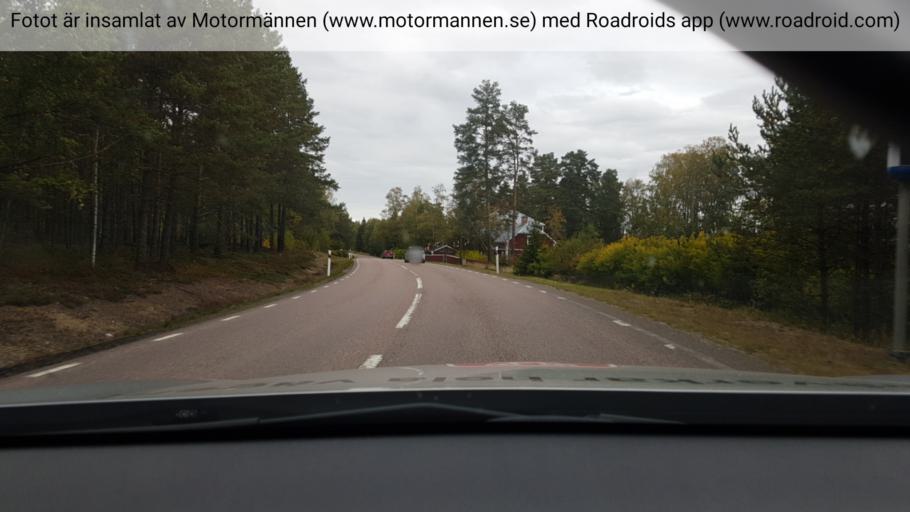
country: SE
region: Gaevleborg
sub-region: Gavle Kommun
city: Valbo
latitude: 60.5703
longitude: 16.9588
